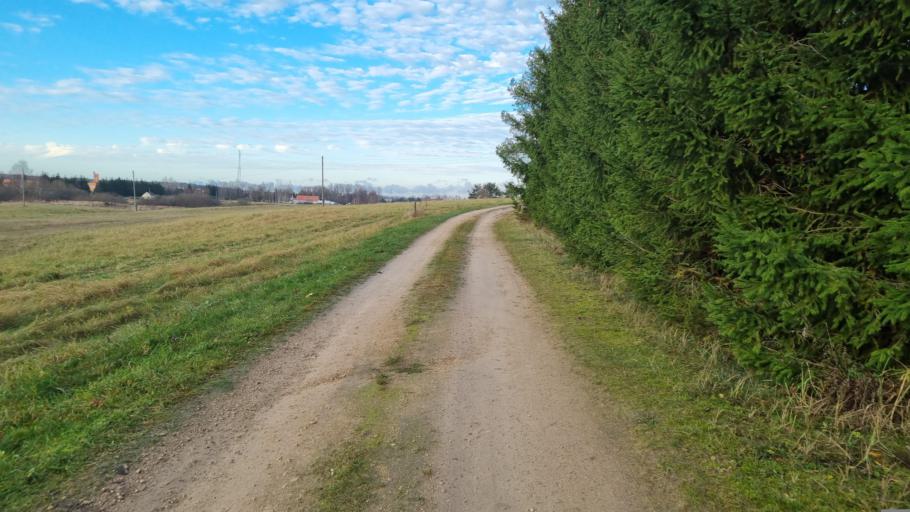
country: LV
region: Kekava
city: Kekava
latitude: 56.7863
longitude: 24.2481
